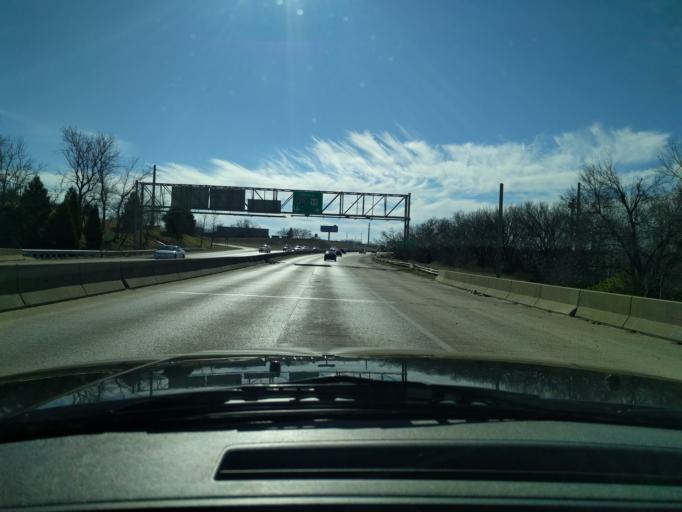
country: US
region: Oklahoma
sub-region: Oklahoma County
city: Nichols Hills
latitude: 35.5274
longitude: -97.5145
